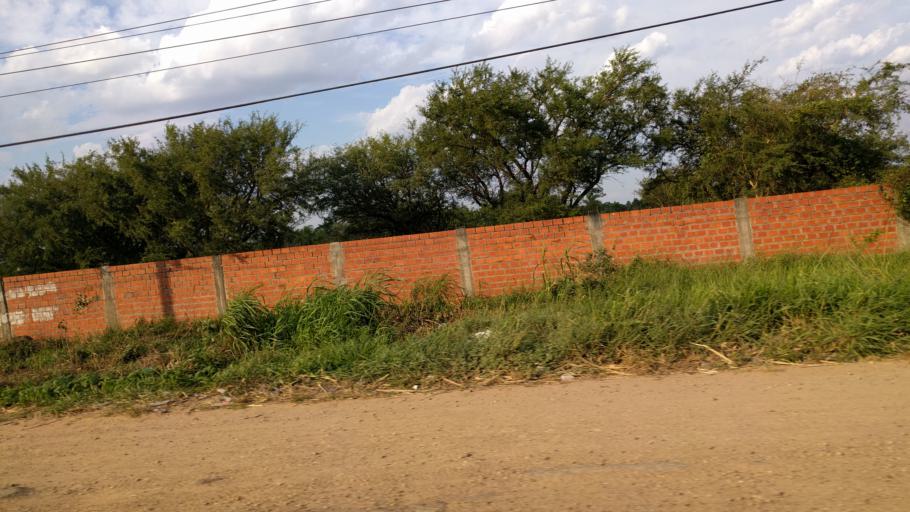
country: BO
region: Santa Cruz
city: Warnes
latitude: -17.5236
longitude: -63.1620
